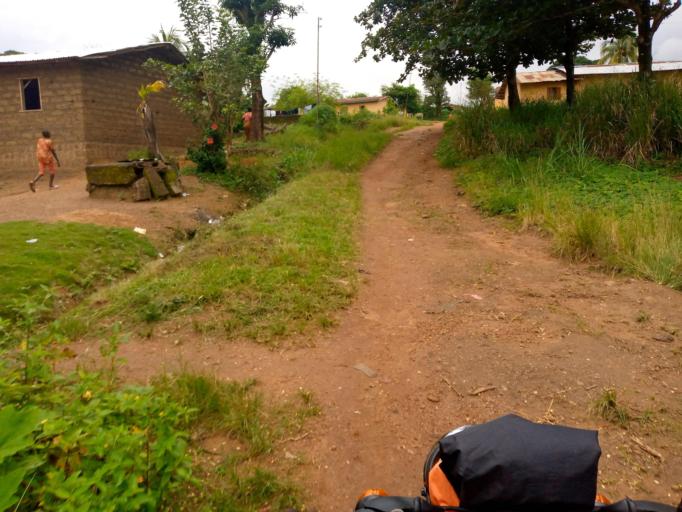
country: SL
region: Eastern Province
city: Kenema
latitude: 7.8687
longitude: -11.1807
